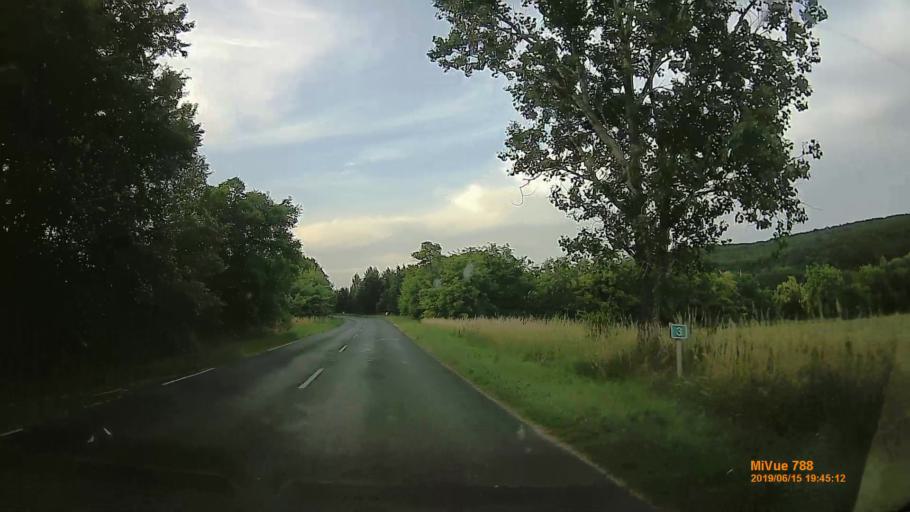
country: HU
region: Veszprem
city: Szentkiralyszabadja
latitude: 47.0071
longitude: 17.9654
